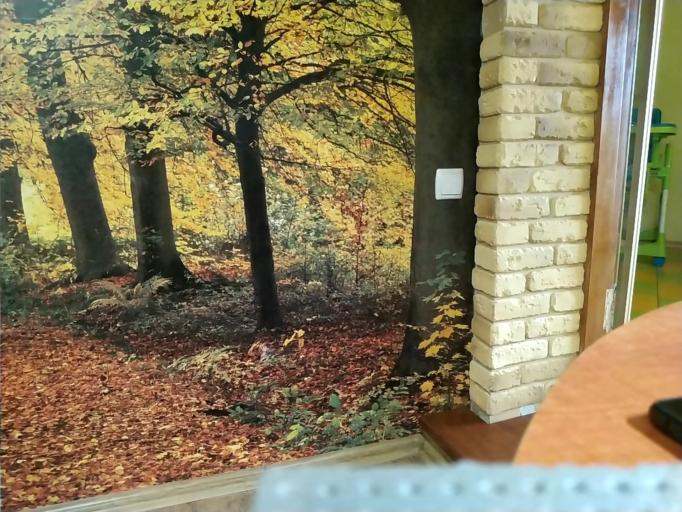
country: RU
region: Vladimir
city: Bavleny
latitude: 56.3658
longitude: 39.5370
